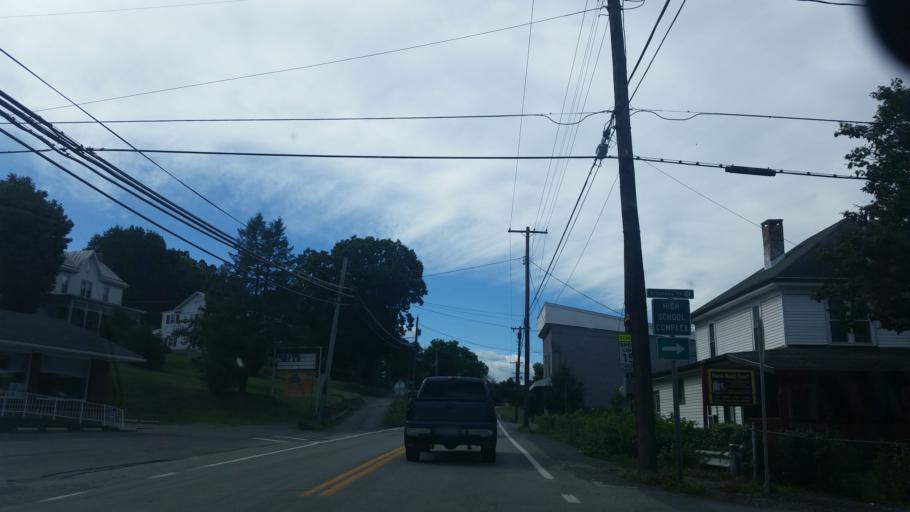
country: US
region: West Virginia
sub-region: Morgan County
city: Berkeley Springs
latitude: 39.6203
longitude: -78.2303
